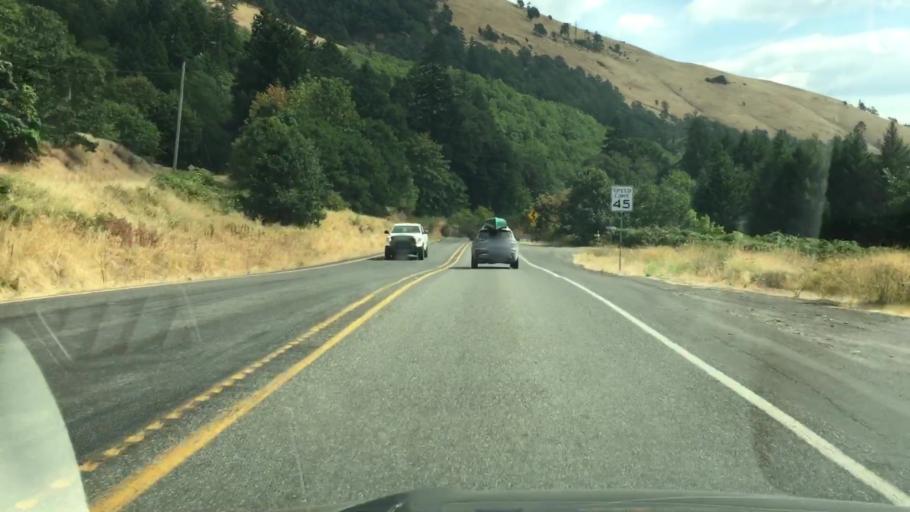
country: US
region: Washington
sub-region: Klickitat County
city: White Salmon
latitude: 45.7568
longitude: -121.5196
